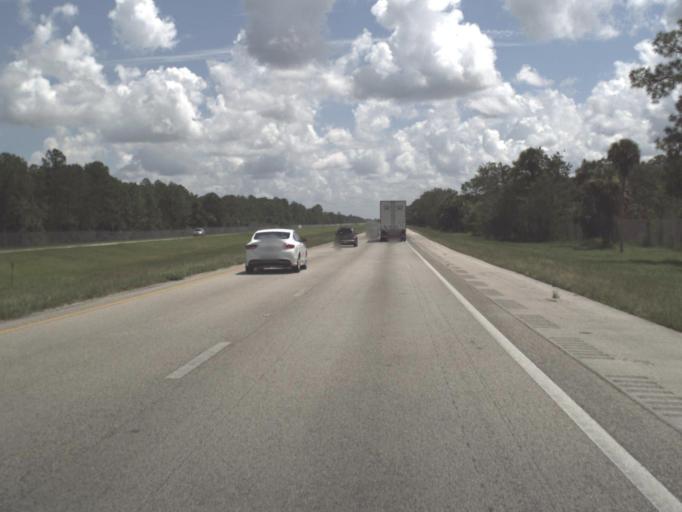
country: US
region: Florida
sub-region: Collier County
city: Orangetree
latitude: 26.1531
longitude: -81.4657
